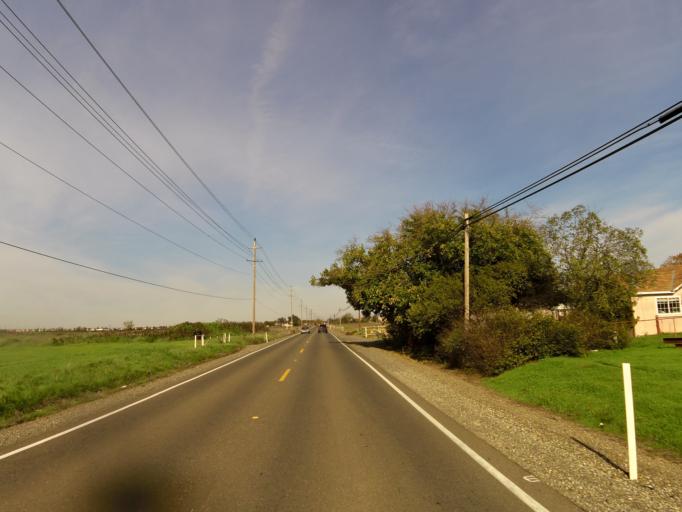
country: US
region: California
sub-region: Sacramento County
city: Laguna
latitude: 38.3673
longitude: -121.4176
